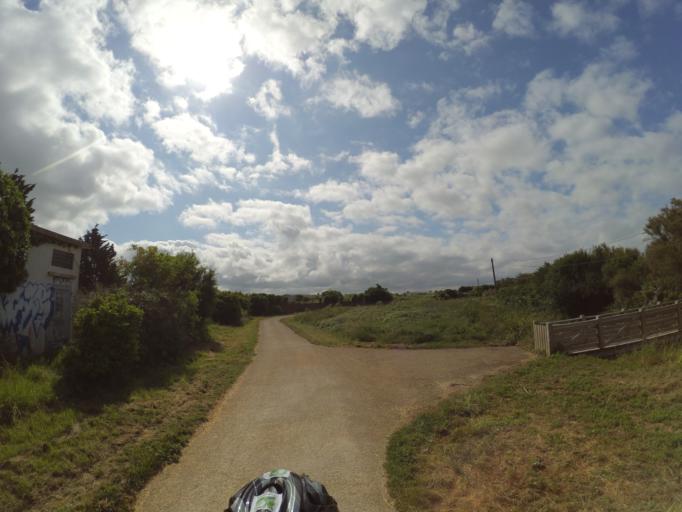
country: FR
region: Poitou-Charentes
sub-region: Departement de la Charente-Maritime
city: Angoulins
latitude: 46.1096
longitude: -1.1181
